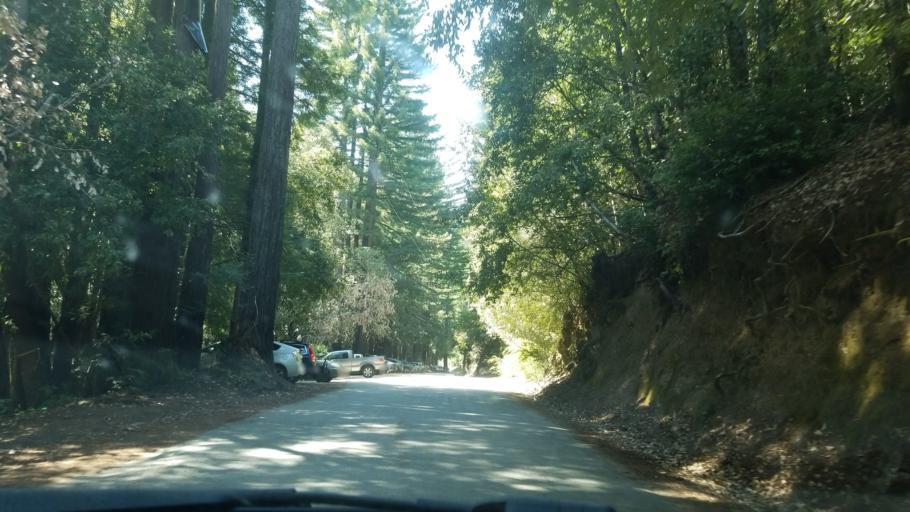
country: US
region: California
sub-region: Santa Cruz County
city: Day Valley
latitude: 37.0817
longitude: -121.8502
